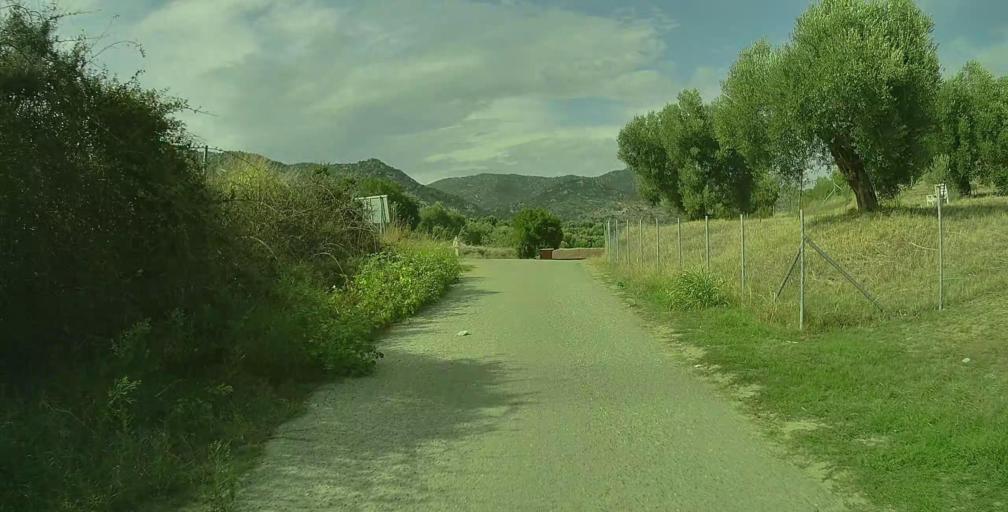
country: GR
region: Central Macedonia
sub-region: Nomos Chalkidikis
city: Sykia
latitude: 40.0329
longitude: 23.9436
